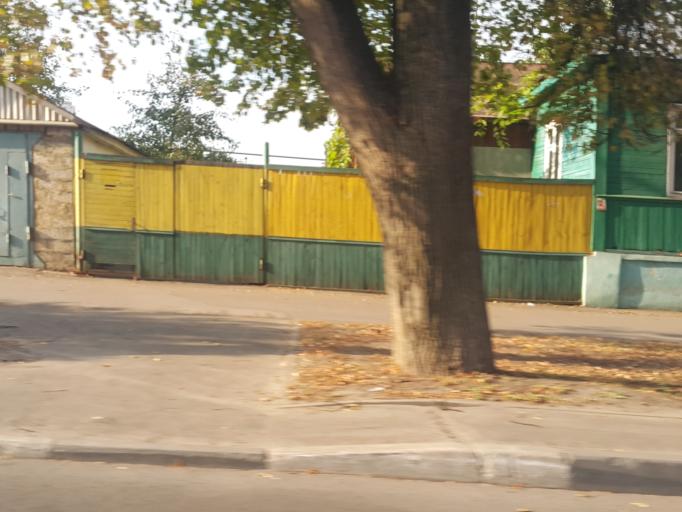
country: RU
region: Tambov
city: Tambov
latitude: 52.7049
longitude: 41.4652
